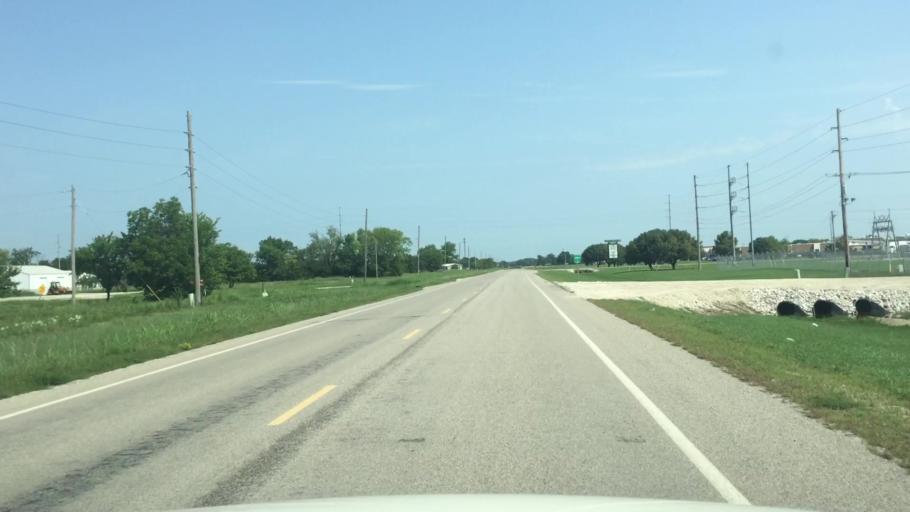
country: US
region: Kansas
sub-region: Montgomery County
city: Coffeyville
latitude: 37.0927
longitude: -95.5862
